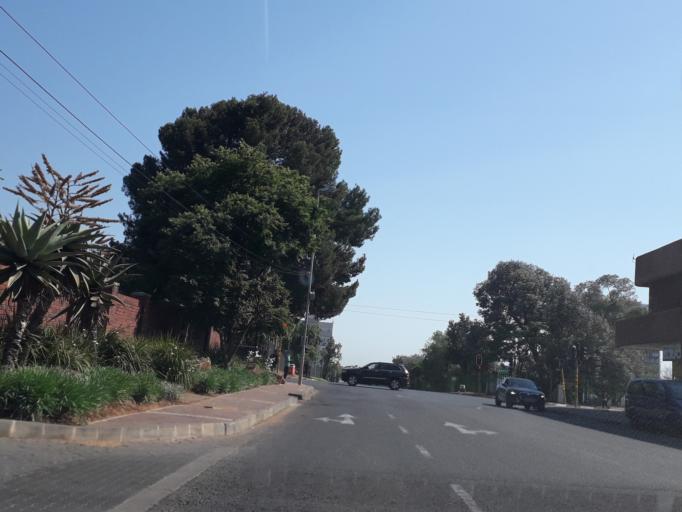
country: ZA
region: Gauteng
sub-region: City of Johannesburg Metropolitan Municipality
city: Johannesburg
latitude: -26.0972
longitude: 28.0034
